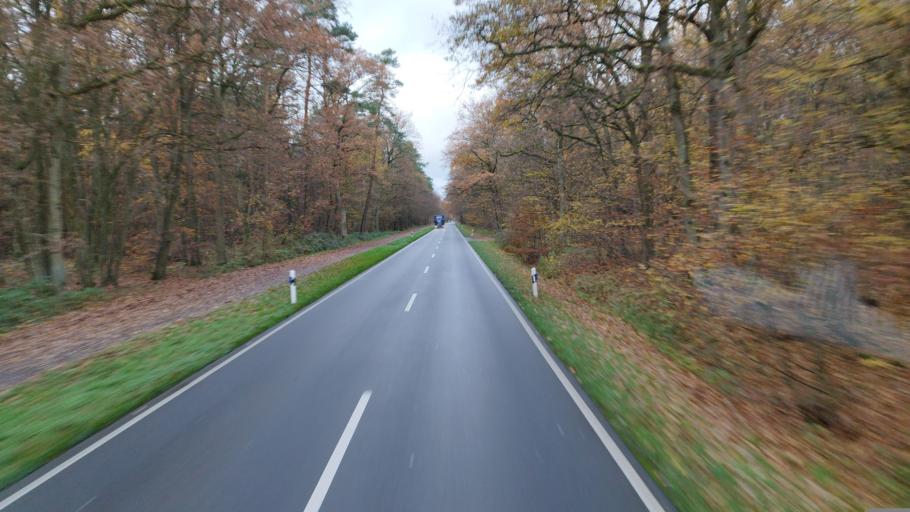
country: DE
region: Rheinland-Pfalz
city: Hatzenbuhl
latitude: 49.1297
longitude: 8.2248
